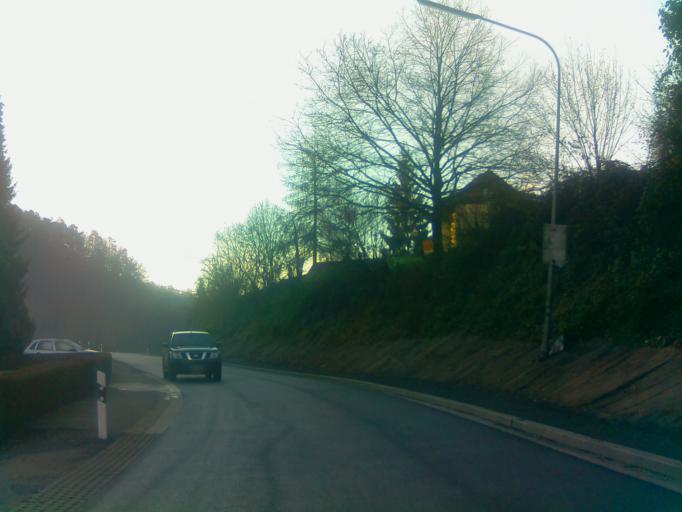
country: DE
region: Hesse
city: Reichelsheim
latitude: 49.6921
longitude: 8.8598
